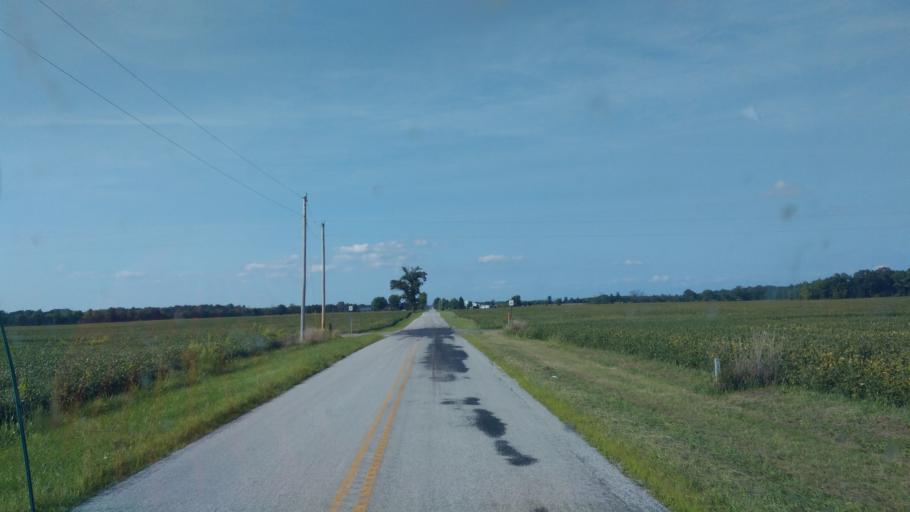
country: US
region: Ohio
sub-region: Hardin County
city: Forest
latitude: 40.7375
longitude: -83.5763
